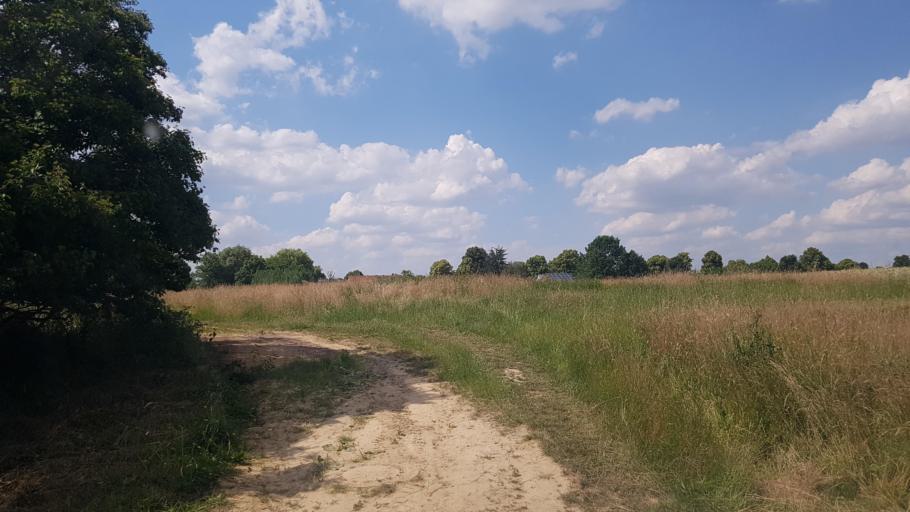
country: DE
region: Brandenburg
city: Finsterwalde
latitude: 51.6872
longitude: 13.7179
